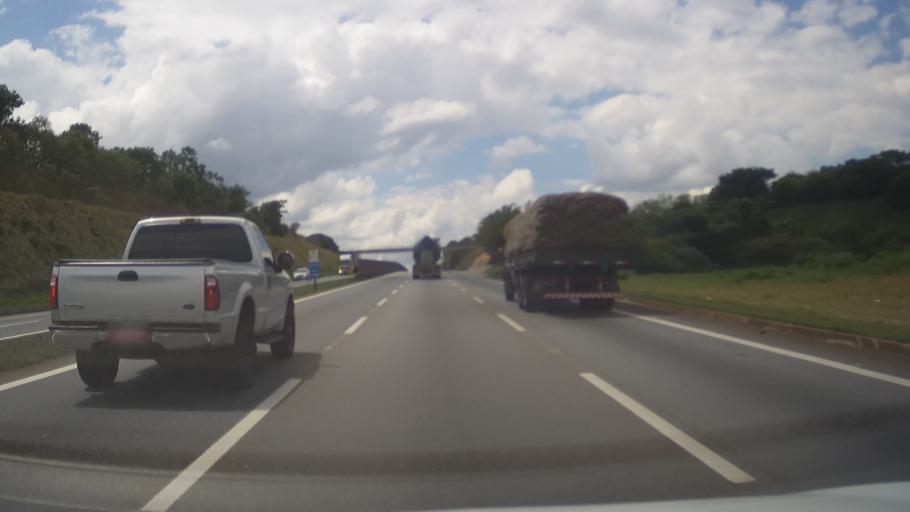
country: BR
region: Minas Gerais
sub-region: Nepomuceno
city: Nepomuceno
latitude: -21.2824
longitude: -45.1400
